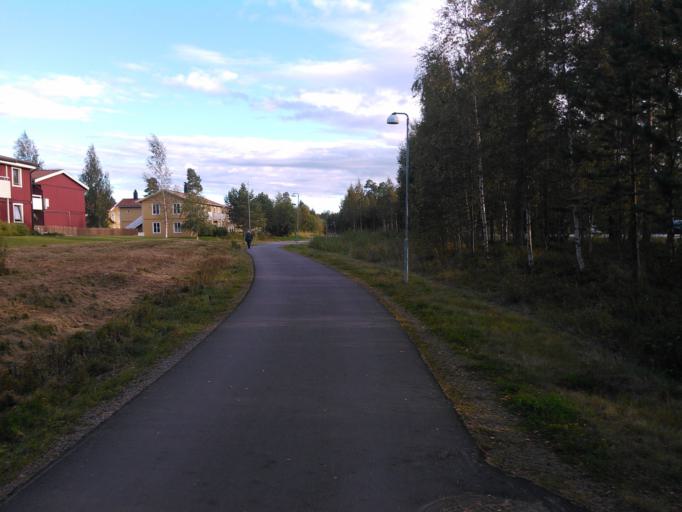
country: SE
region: Vaesterbotten
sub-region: Umea Kommun
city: Ersmark
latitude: 63.8084
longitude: 20.3357
